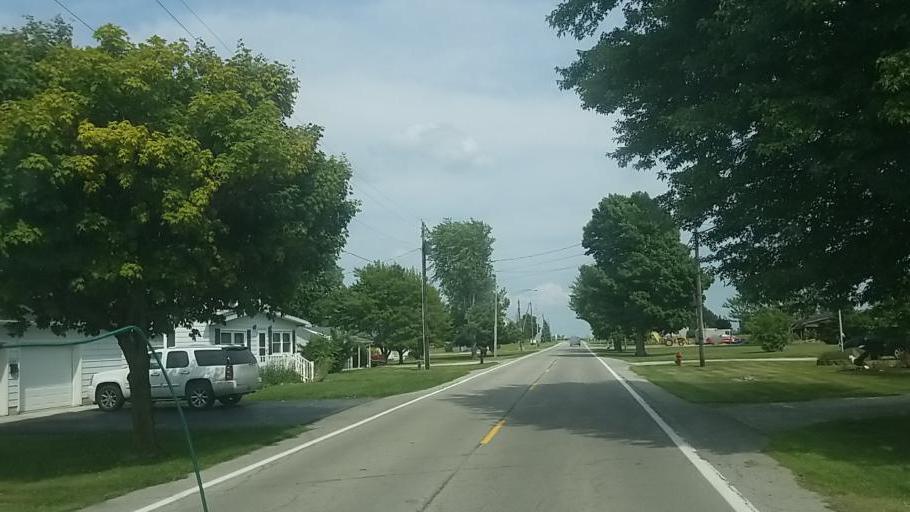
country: US
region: Ohio
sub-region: Hardin County
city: Forest
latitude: 40.8018
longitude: -83.5031
